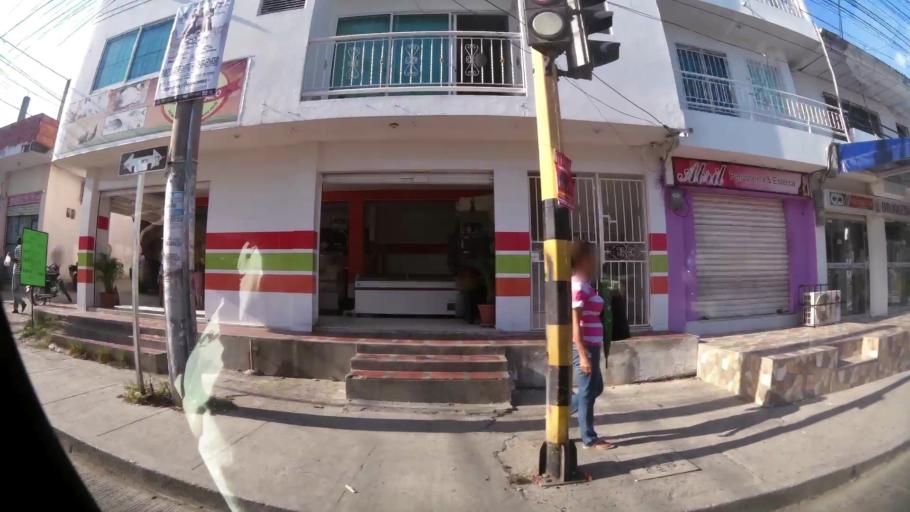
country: CO
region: Bolivar
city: Cartagena
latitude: 10.4003
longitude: -75.5013
